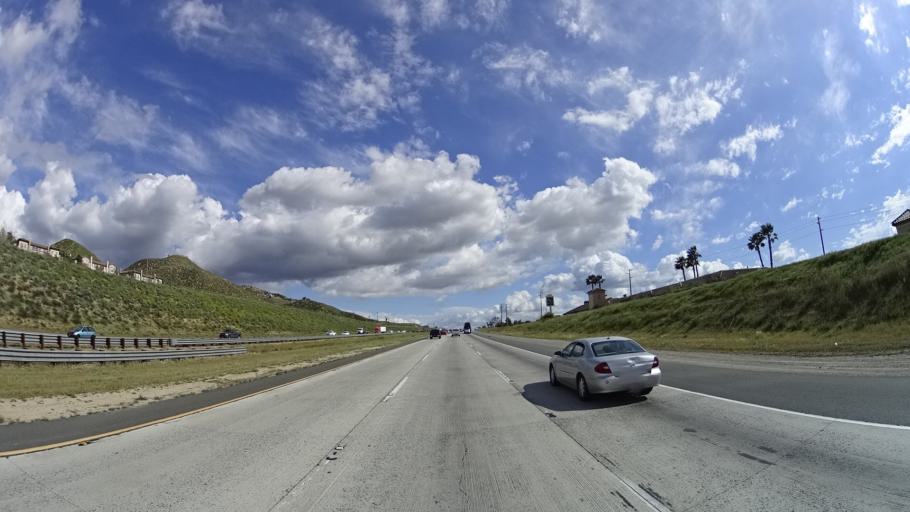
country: US
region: California
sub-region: Riverside County
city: Sedco Hills
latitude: 33.6571
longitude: -117.2941
